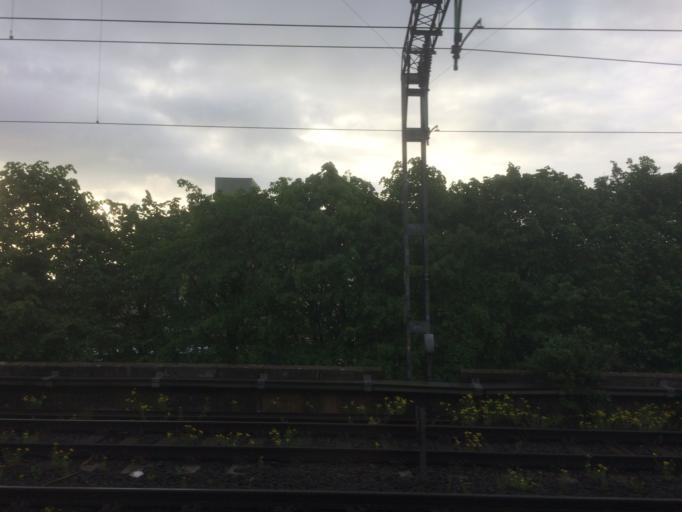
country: GB
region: Scotland
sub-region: Glasgow City
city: Glasgow
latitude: 55.8506
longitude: -4.2603
